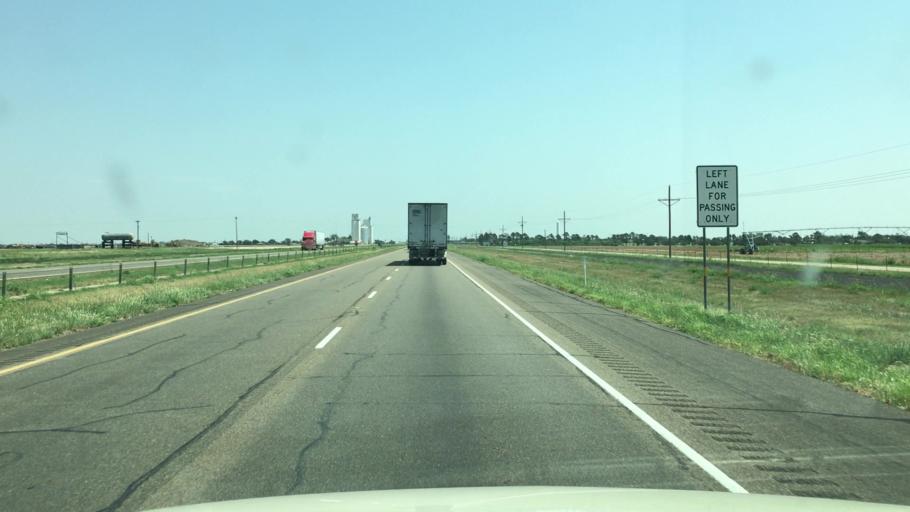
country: US
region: Texas
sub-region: Potter County
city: Bushland
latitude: 35.1917
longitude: -102.0849
